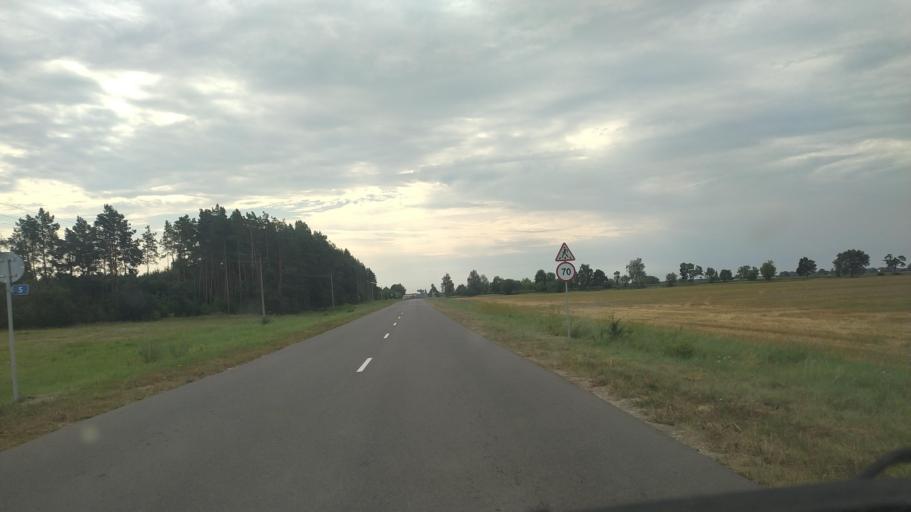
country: BY
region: Brest
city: Byaroza
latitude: 52.5601
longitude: 24.9102
